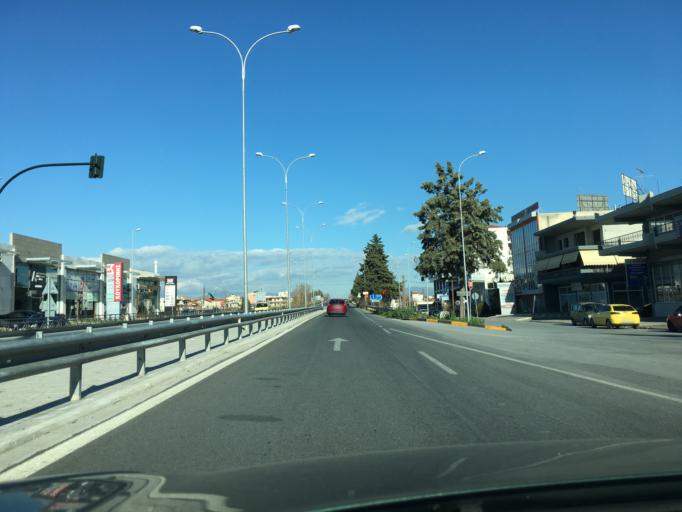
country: GR
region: Thessaly
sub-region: Nomos Larisis
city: Larisa
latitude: 39.6284
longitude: 22.4328
